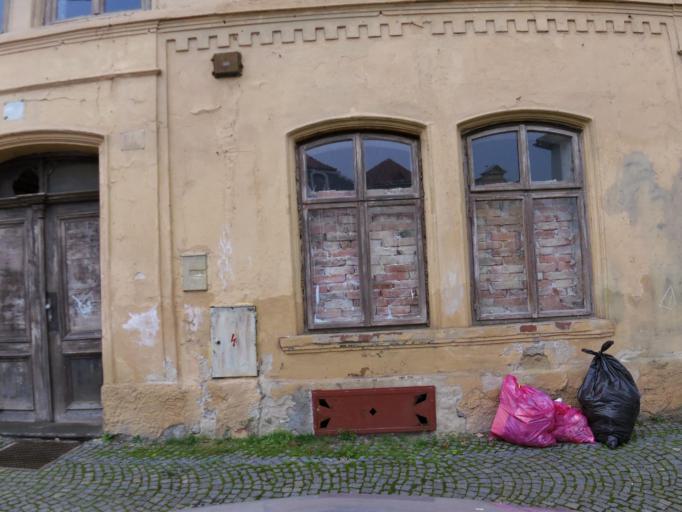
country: CZ
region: Ustecky
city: Zatec
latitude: 50.3294
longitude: 13.5467
